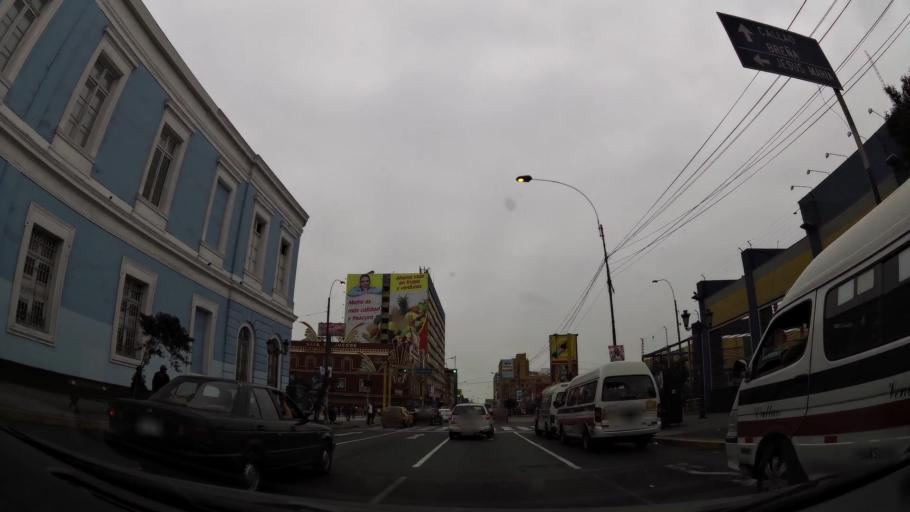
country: PE
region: Lima
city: Lima
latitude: -12.0544
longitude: -77.0415
